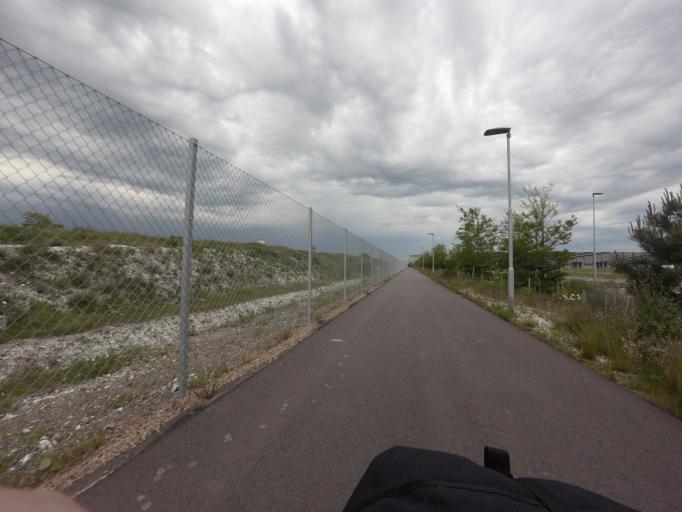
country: SE
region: Skane
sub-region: Malmo
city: Malmoe
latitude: 55.6344
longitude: 13.0064
